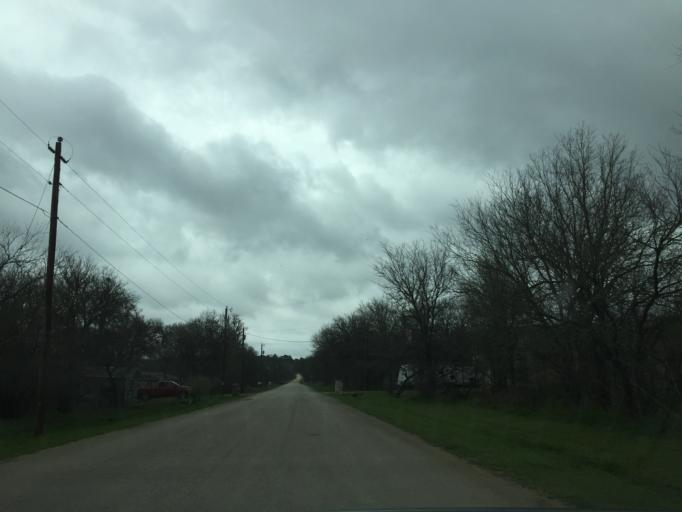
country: US
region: Texas
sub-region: Bastrop County
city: Bastrop
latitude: 30.0897
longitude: -97.3129
